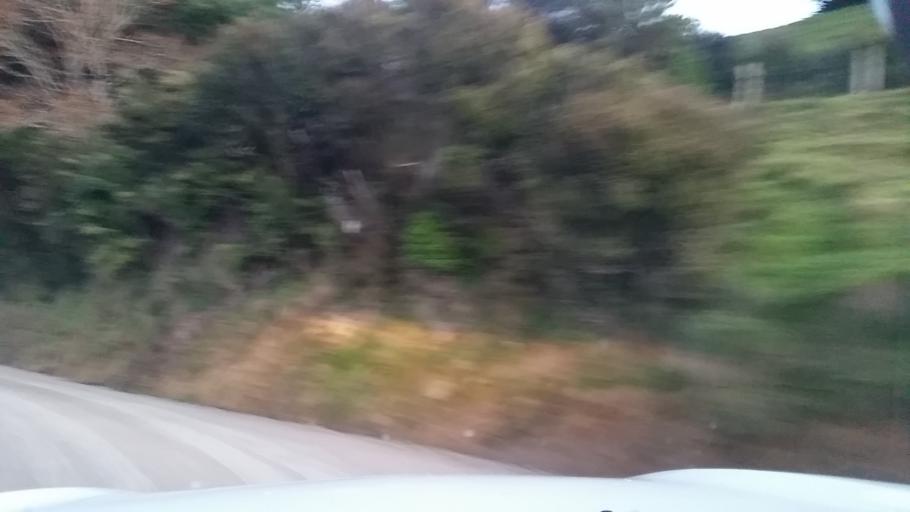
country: NZ
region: Manawatu-Wanganui
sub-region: Wanganui District
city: Wanganui
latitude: -39.7668
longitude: 174.8713
